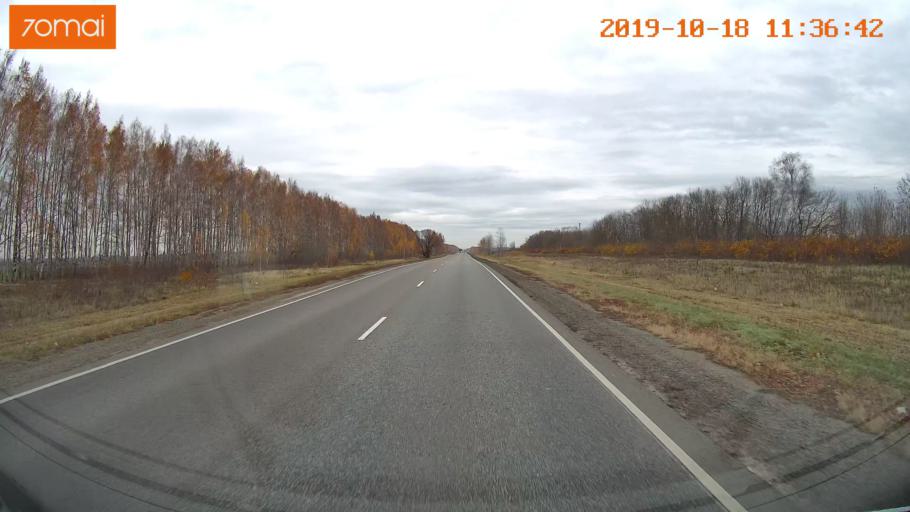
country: RU
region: Rjazan
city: Oktyabr'skiy
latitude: 54.1438
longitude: 38.8131
